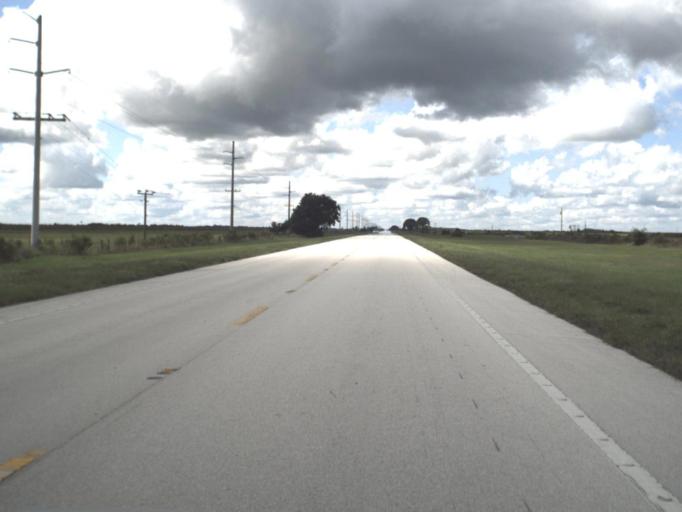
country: US
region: Florida
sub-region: Highlands County
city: Placid Lakes
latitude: 27.2097
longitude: -81.5674
